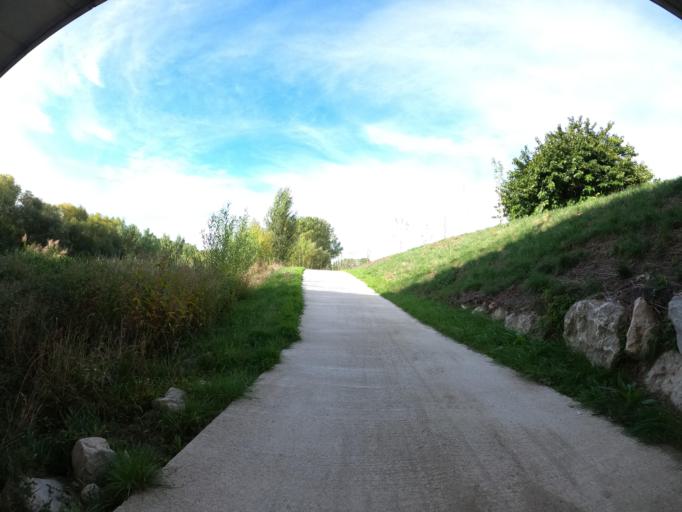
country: ES
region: Navarre
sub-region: Provincia de Navarra
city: Oltza
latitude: 42.8147
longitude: -1.7485
